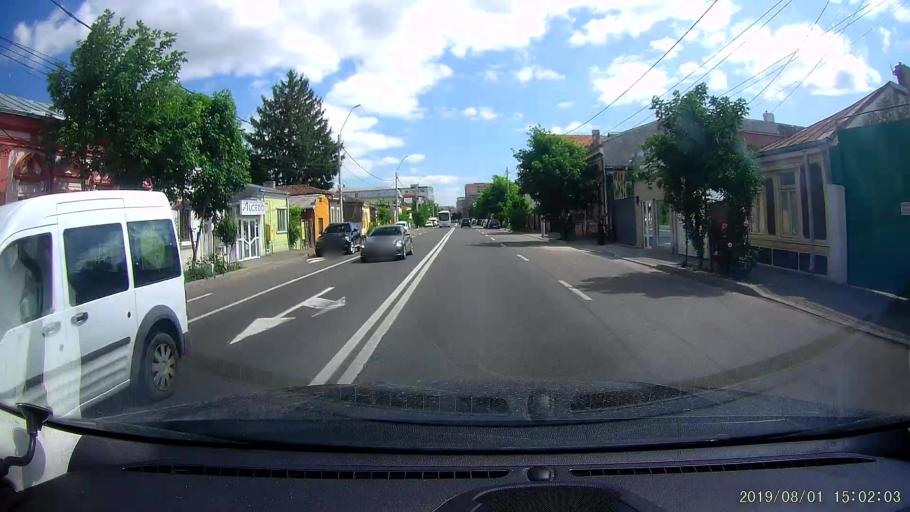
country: RO
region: Braila
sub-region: Municipiul Braila
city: Braila
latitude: 45.2687
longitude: 27.9606
